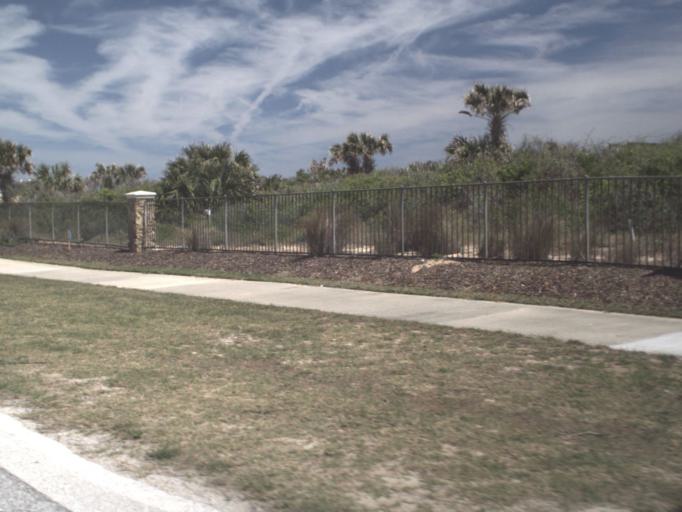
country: US
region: Florida
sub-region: Flagler County
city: Palm Coast
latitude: 29.5578
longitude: -81.1658
